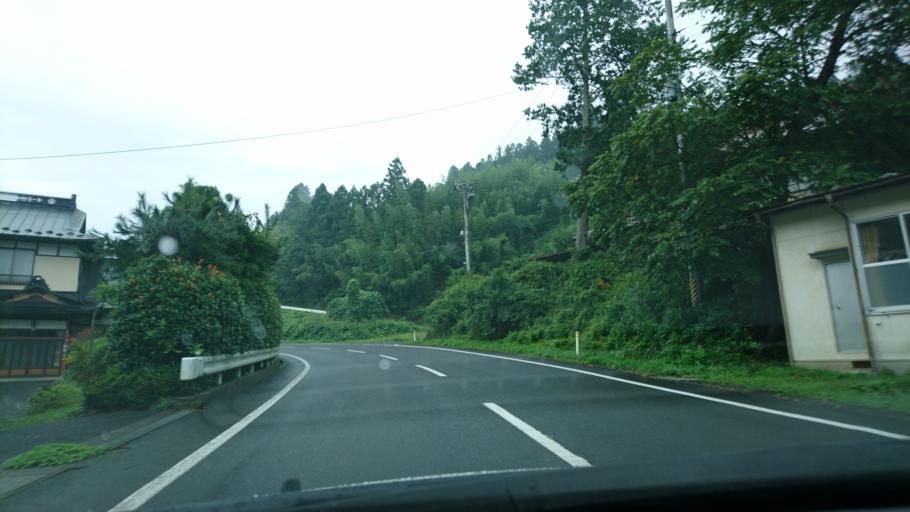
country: JP
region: Iwate
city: Ichinoseki
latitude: 38.8810
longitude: 141.2631
